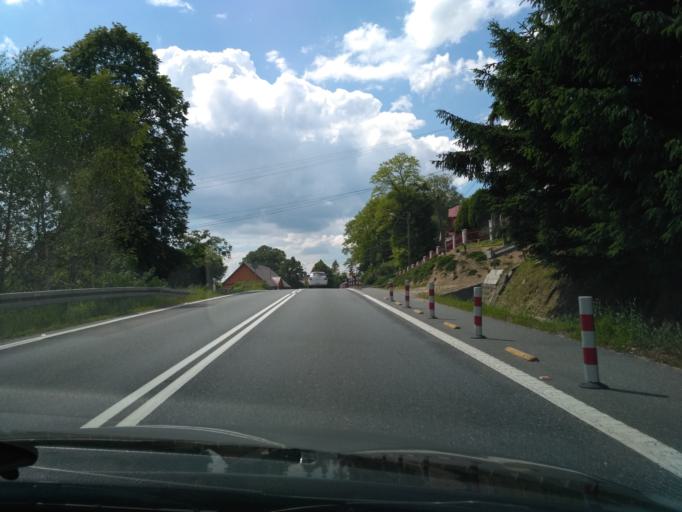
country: PL
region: Subcarpathian Voivodeship
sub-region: Powiat strzyzowski
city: Jawornik
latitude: 49.8051
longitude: 21.8975
